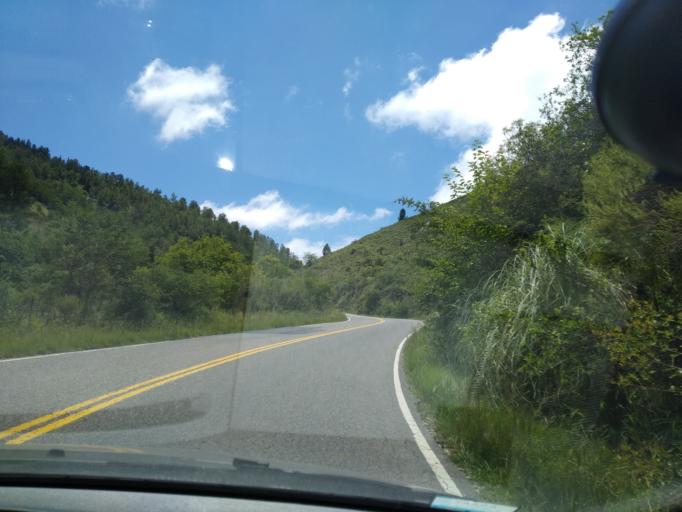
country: AR
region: Cordoba
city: Cuesta Blanca
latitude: -31.6037
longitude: -64.5518
